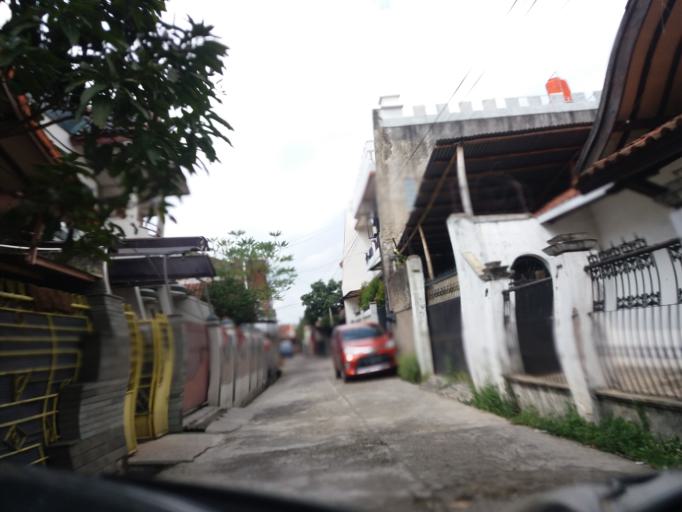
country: ID
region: West Java
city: Bandung
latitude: -6.9257
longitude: 107.6587
